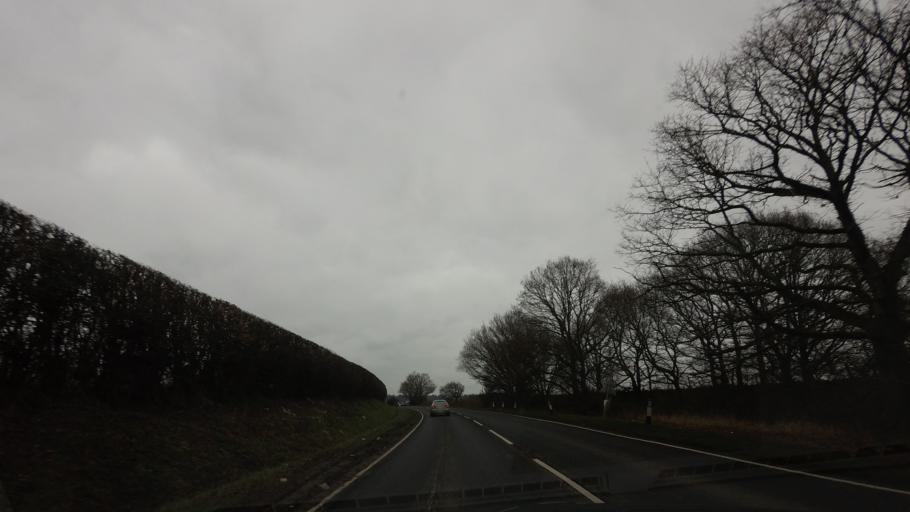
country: GB
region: England
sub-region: Kent
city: Marden
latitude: 51.2065
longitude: 0.5178
